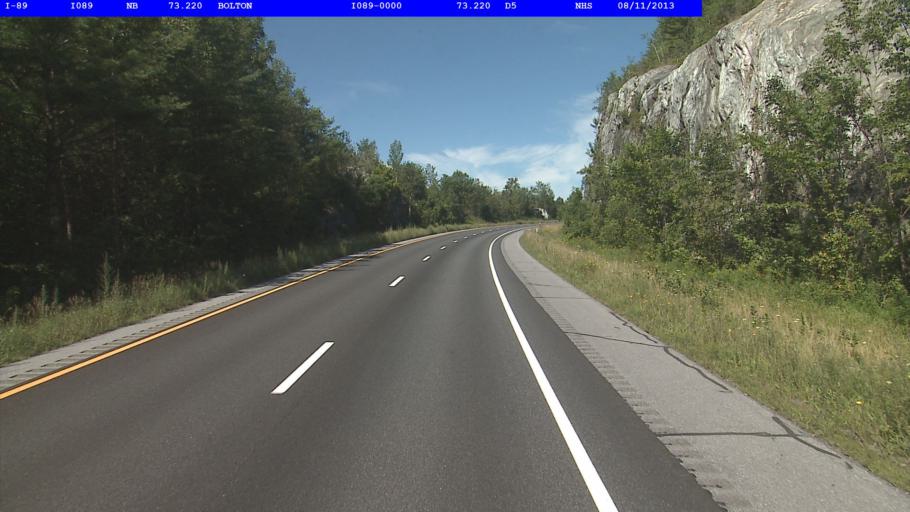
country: US
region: Vermont
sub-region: Chittenden County
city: Jericho
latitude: 44.3833
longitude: -72.9297
